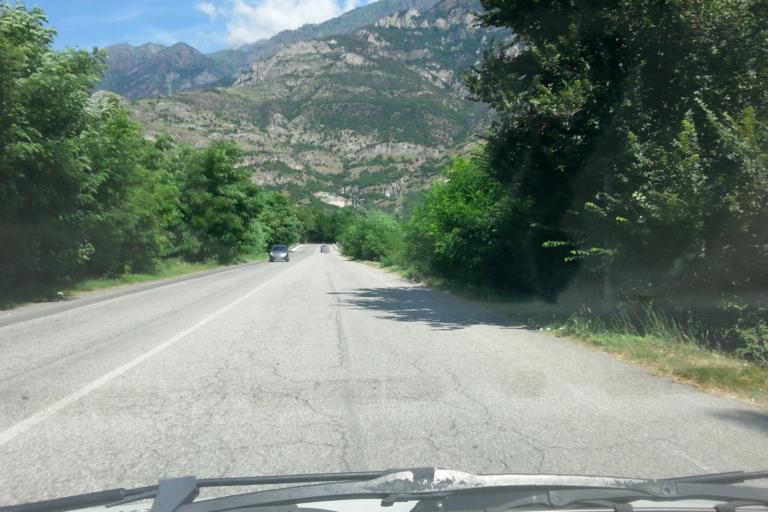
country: IT
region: Piedmont
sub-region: Provincia di Torino
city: Bussoleno
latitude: 45.1355
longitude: 7.1365
